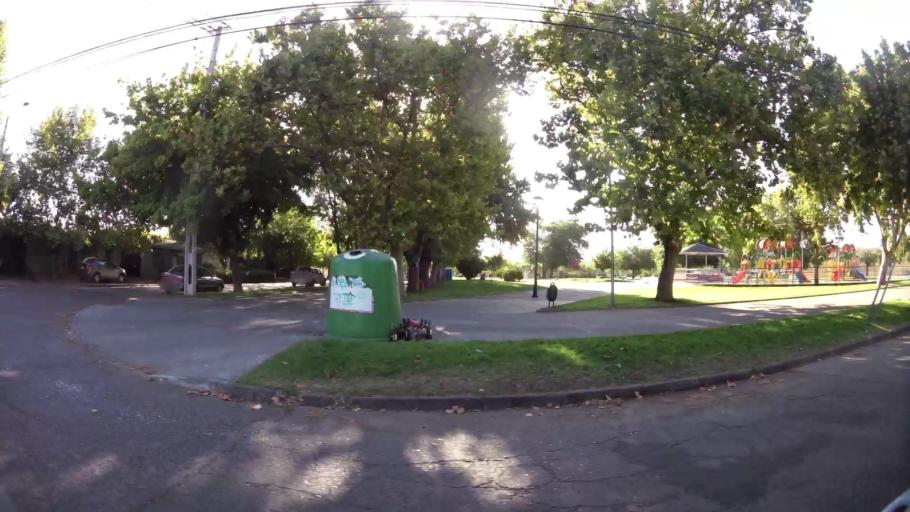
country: CL
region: Maule
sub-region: Provincia de Talca
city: Talca
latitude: -35.4349
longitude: -71.6543
